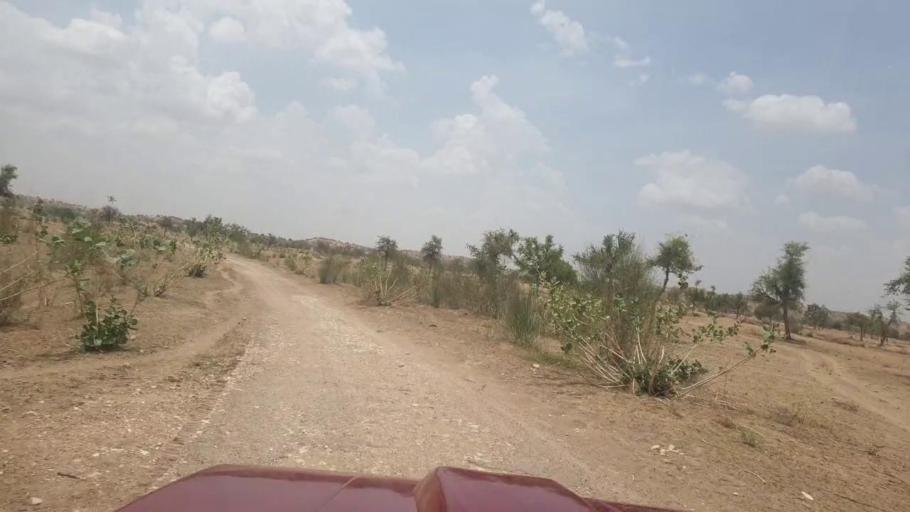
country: PK
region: Sindh
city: Islamkot
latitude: 25.1972
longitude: 70.4320
